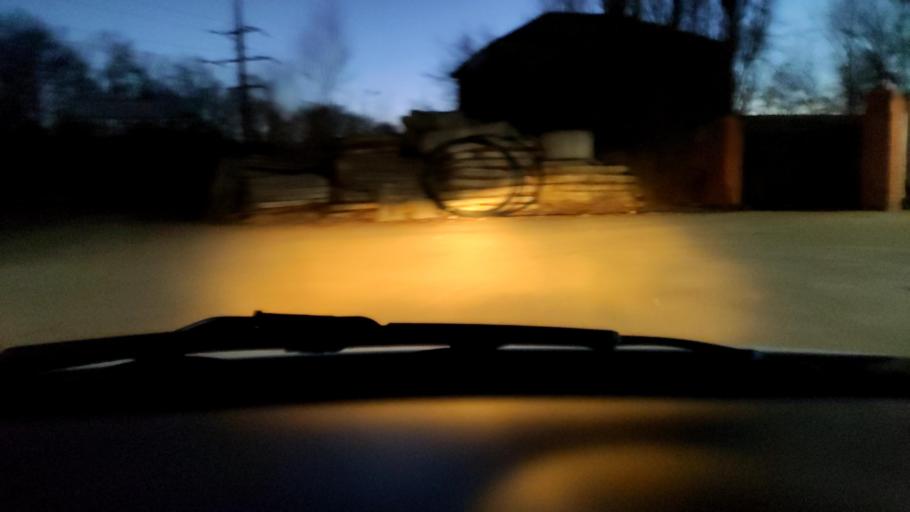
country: RU
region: Voronezj
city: Voronezh
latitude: 51.6685
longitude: 39.1342
